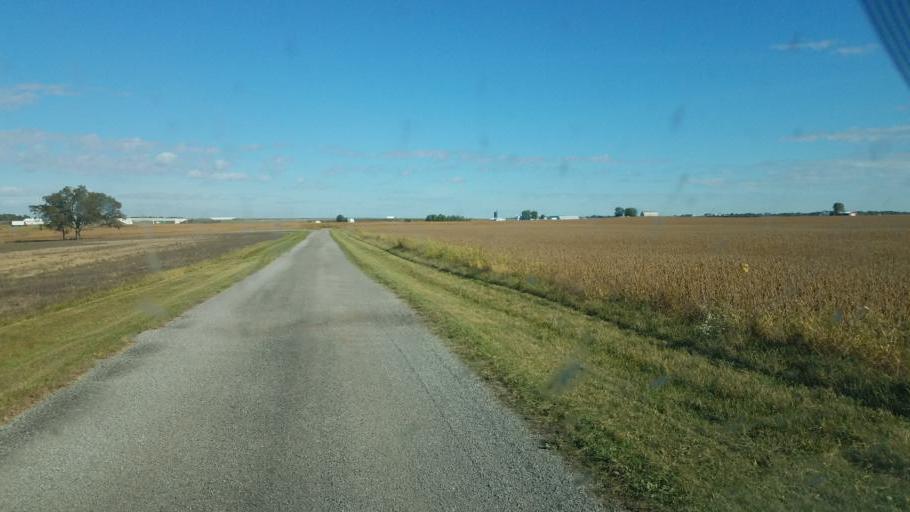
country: US
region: Ohio
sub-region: Wyandot County
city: Upper Sandusky
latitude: 40.7941
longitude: -83.2331
